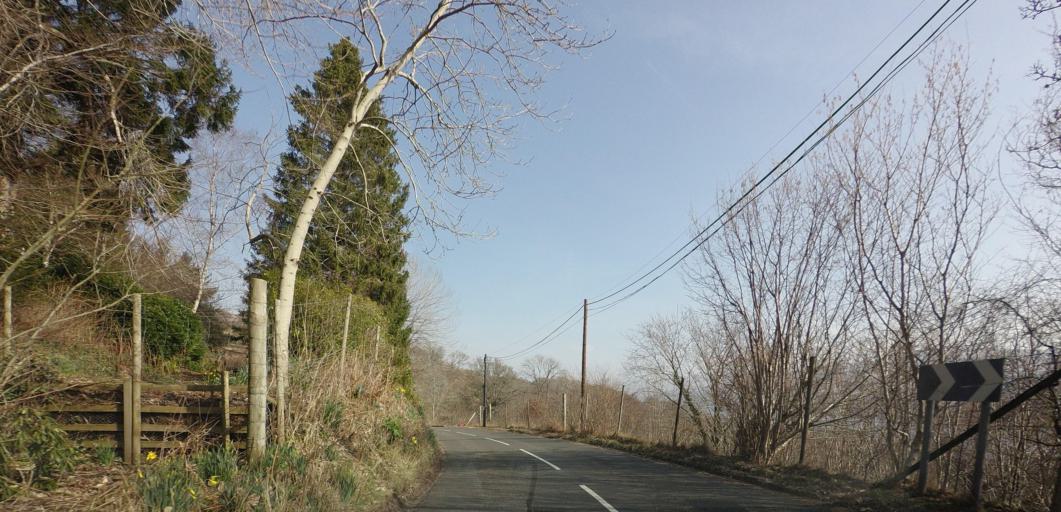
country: GB
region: Scotland
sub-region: Stirling
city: Callander
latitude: 56.4841
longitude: -4.2947
